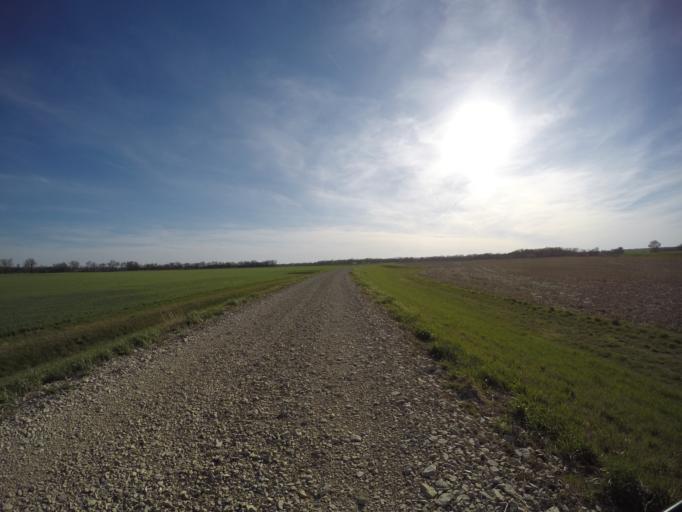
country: US
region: Kansas
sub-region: Saline County
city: Salina
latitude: 38.8608
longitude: -97.6251
